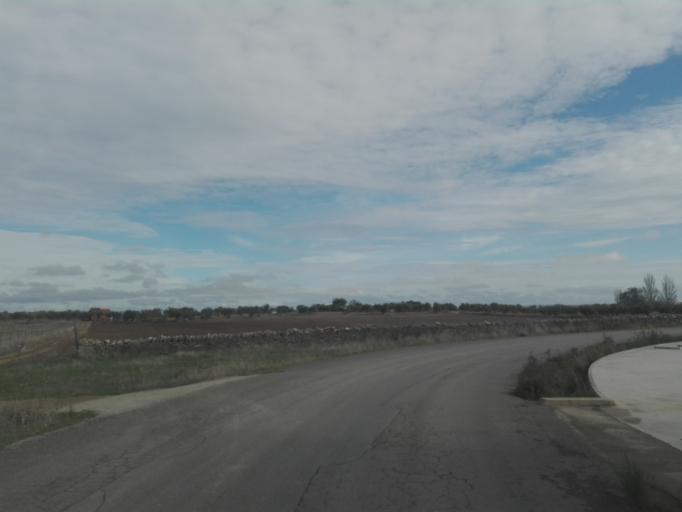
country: ES
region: Extremadura
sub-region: Provincia de Badajoz
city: Villagarcia de la Torre
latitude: 38.2937
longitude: -6.0871
